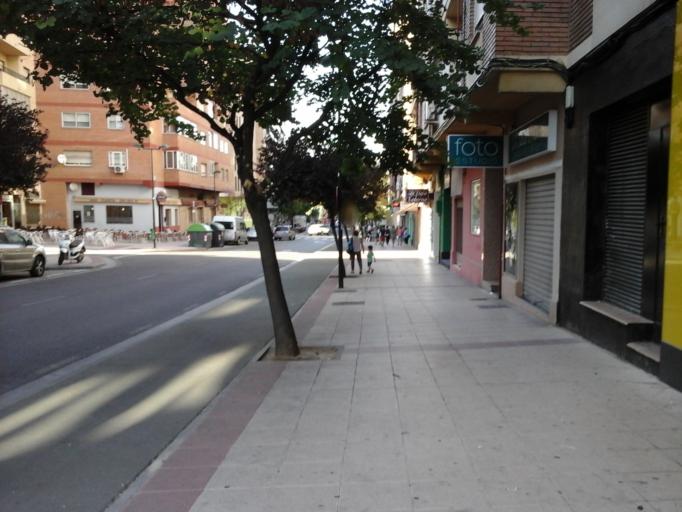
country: ES
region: Aragon
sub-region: Provincia de Zaragoza
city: Zaragoza
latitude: 41.6332
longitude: -0.8755
